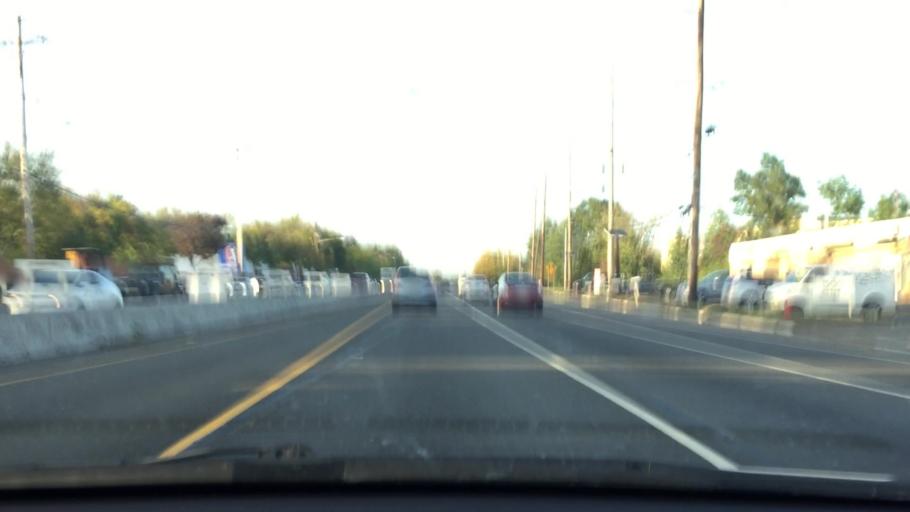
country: US
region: New Jersey
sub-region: Bergen County
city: Paramus
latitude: 40.9405
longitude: -74.0713
